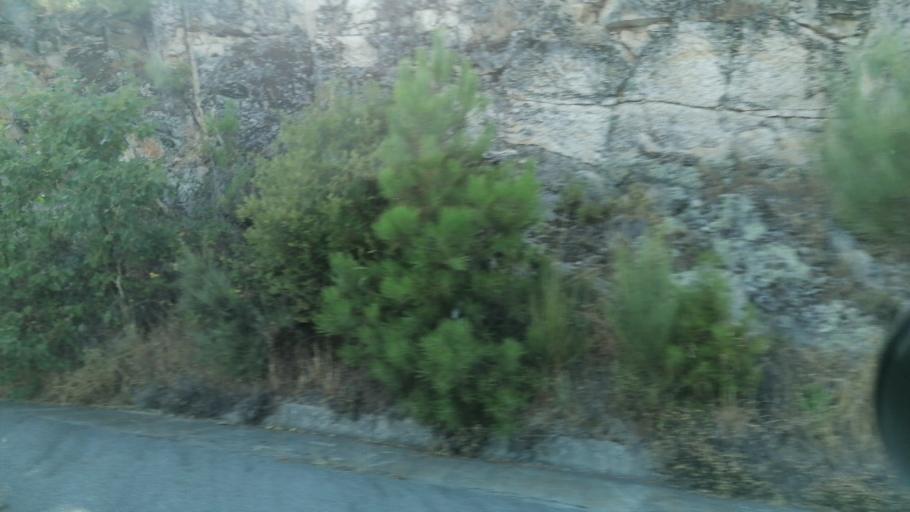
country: PT
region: Vila Real
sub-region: Sabrosa
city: Sabrosa
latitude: 41.3641
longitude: -7.5542
